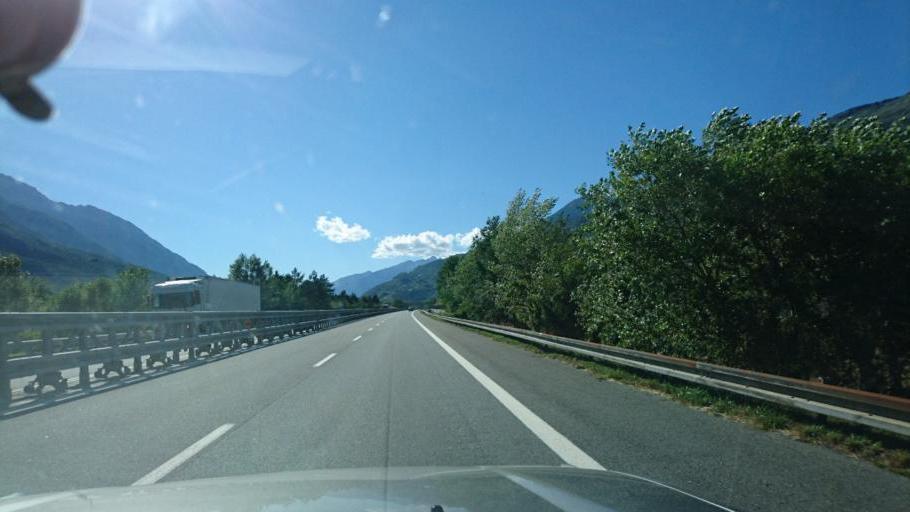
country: IT
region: Aosta Valley
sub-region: Valle d'Aosta
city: Chambave
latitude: 45.7414
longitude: 7.5274
